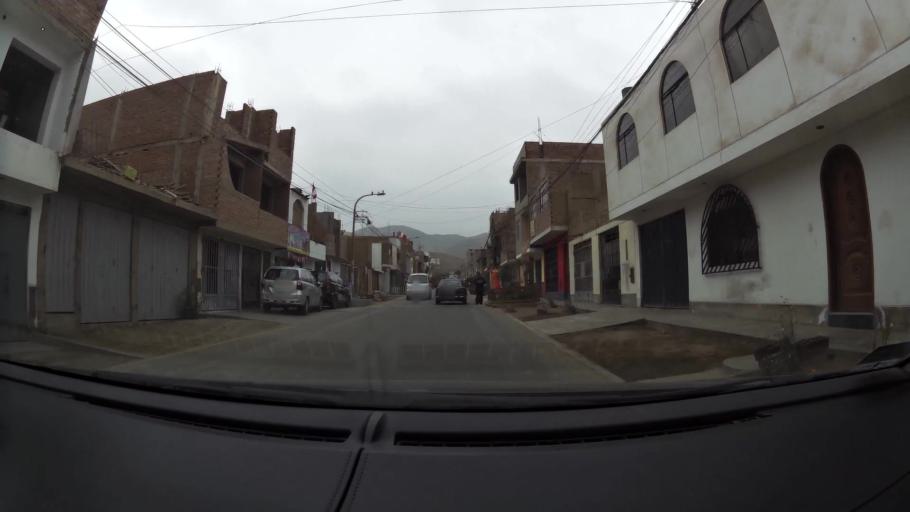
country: PE
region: Lima
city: Ventanilla
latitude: -11.9247
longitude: -77.0821
